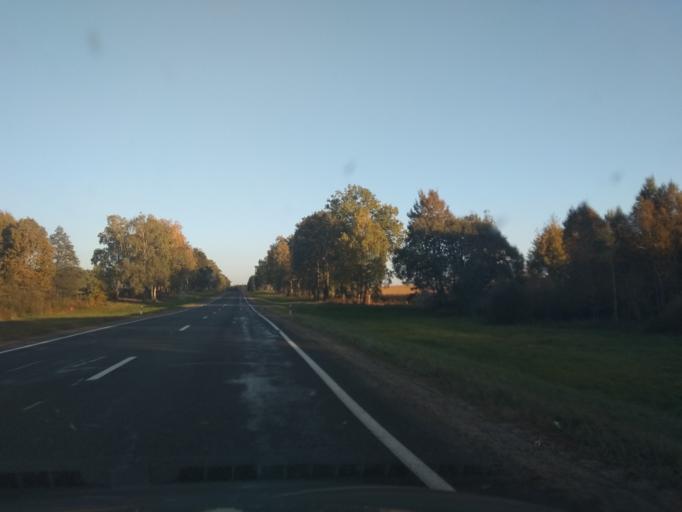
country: BY
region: Grodnenskaya
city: Vawkavysk
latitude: 53.1440
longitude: 24.6166
